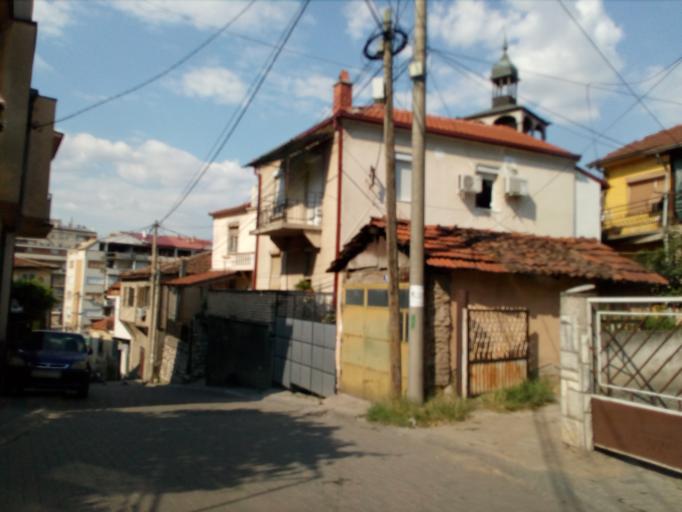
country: MK
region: Veles
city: Veles
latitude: 41.7139
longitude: 21.7835
